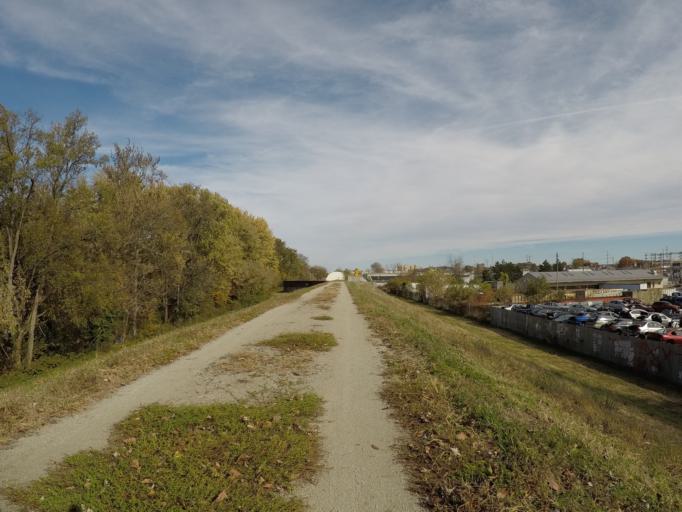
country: US
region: West Virginia
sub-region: Cabell County
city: Huntington
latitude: 38.4191
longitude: -82.4642
